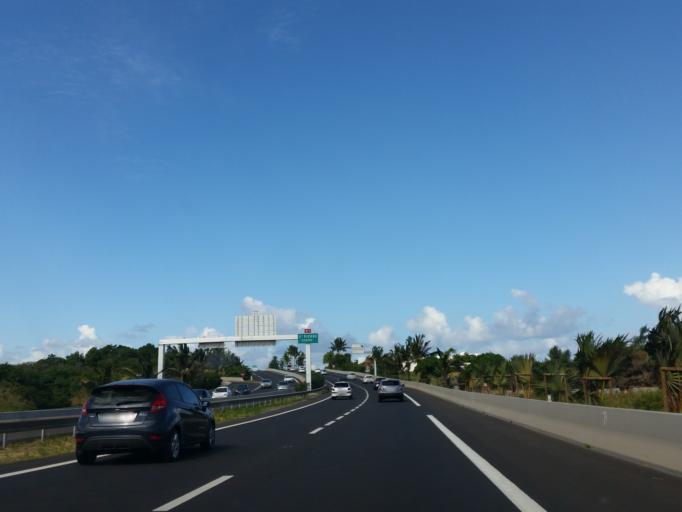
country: RE
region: Reunion
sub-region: Reunion
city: Saint-Pierre
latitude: -21.3297
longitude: 55.4537
